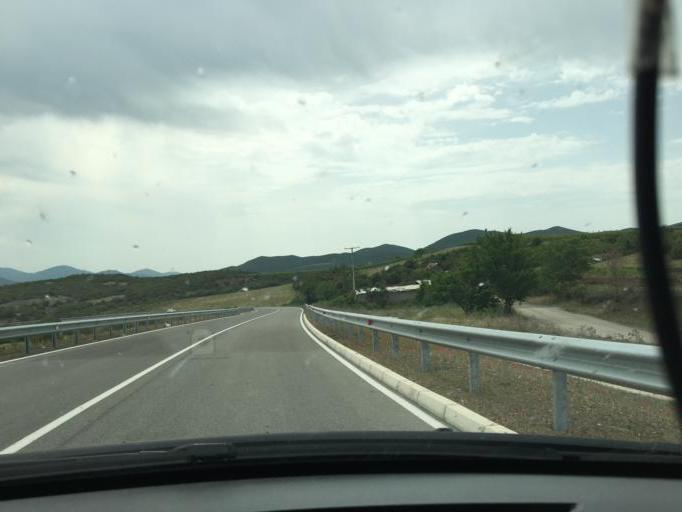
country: MK
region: Gevgelija
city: Miravci
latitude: 41.3016
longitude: 22.4360
